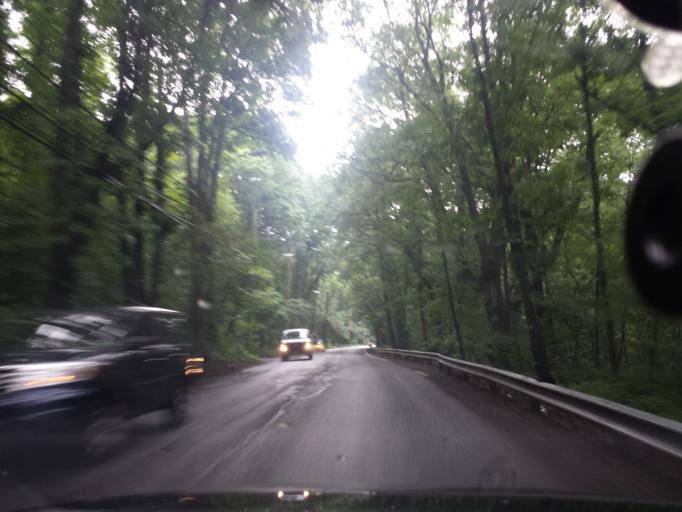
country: US
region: New York
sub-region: Richmond County
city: Staten Island
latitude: 40.5815
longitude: -74.1289
